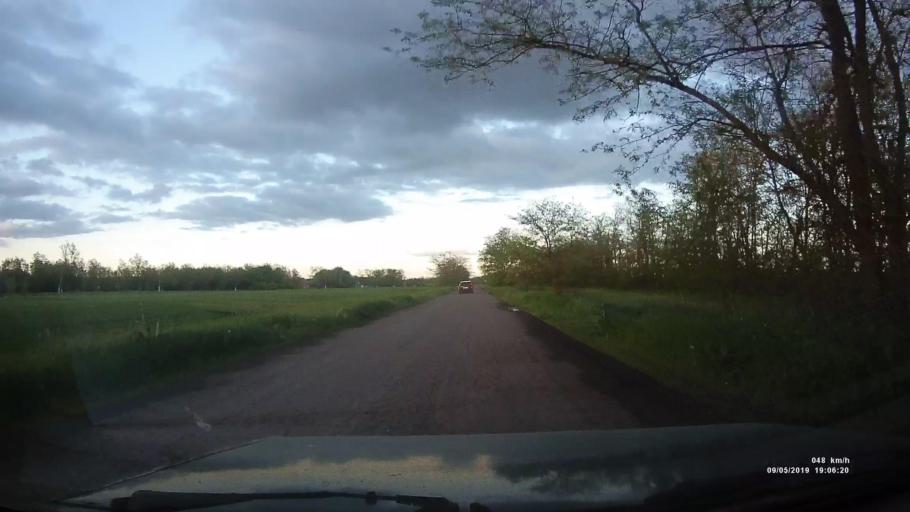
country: RU
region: Krasnodarskiy
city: Kanelovskaya
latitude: 46.7384
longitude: 39.1898
